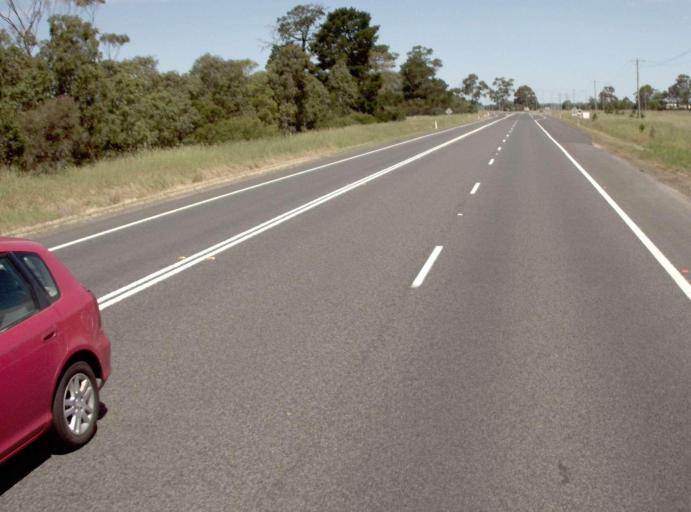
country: AU
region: Victoria
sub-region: Wellington
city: Sale
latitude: -38.0632
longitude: 147.0717
